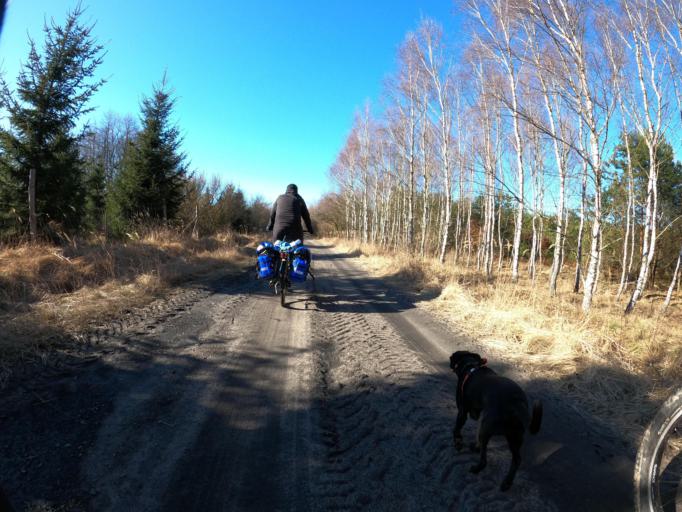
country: PL
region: West Pomeranian Voivodeship
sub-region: Powiat szczecinecki
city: Borne Sulinowo
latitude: 53.5474
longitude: 16.5606
